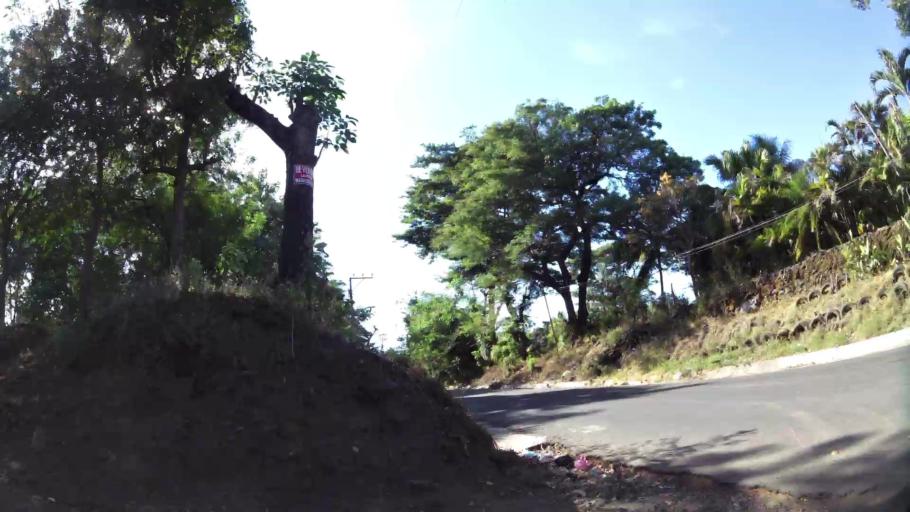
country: SV
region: San Miguel
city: San Miguel
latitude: 13.4773
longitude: -88.1953
